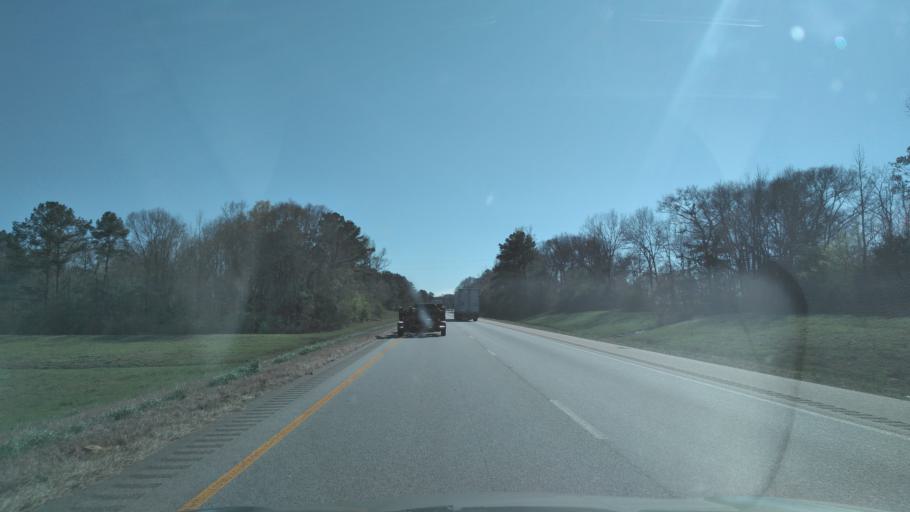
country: US
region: Alabama
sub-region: Lowndes County
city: Fort Deposit
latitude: 31.9724
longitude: -86.5353
